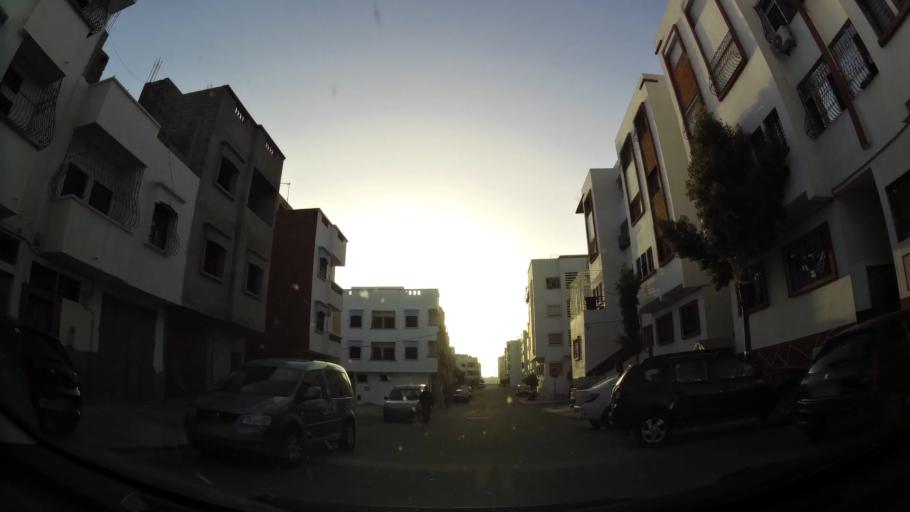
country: MA
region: Oued ed Dahab-Lagouira
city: Dakhla
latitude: 30.3977
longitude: -9.5595
